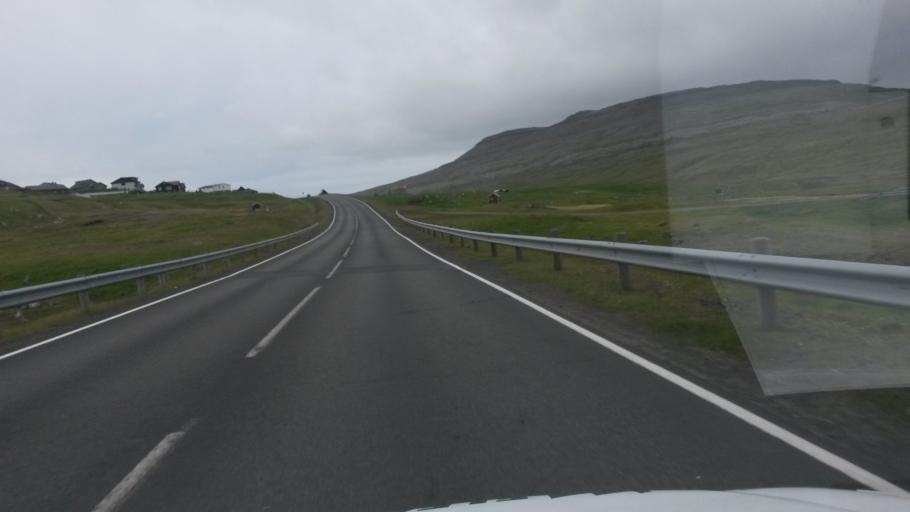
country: FO
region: Streymoy
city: Hoyvik
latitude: 62.0016
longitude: -6.8399
